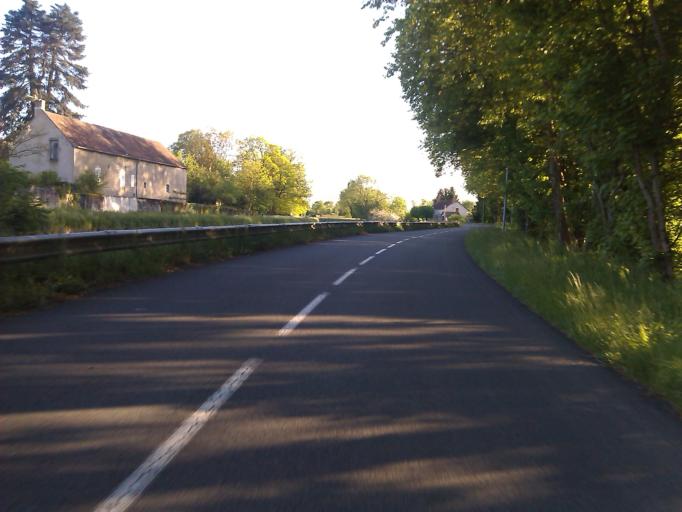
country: FR
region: Bourgogne
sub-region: Departement de Saone-et-Loire
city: Palinges
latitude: 46.5646
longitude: 4.2227
